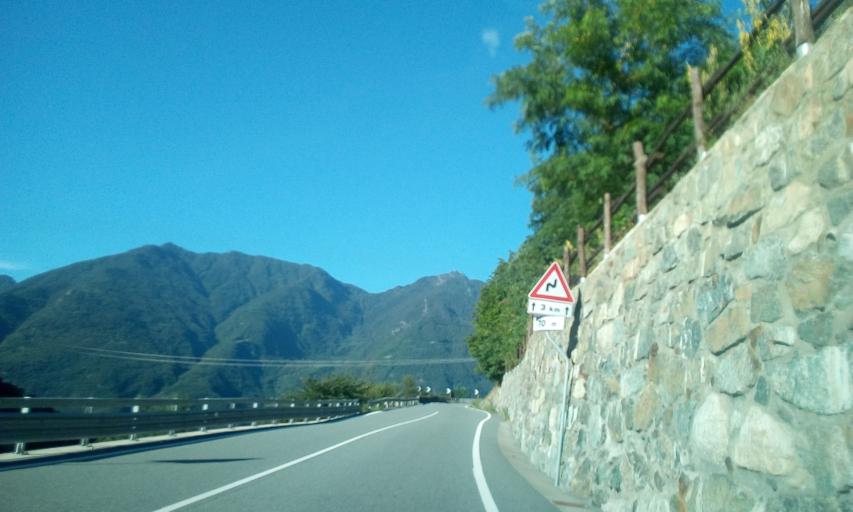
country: IT
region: Aosta Valley
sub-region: Valle d'Aosta
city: Verres
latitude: 45.6728
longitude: 7.6950
